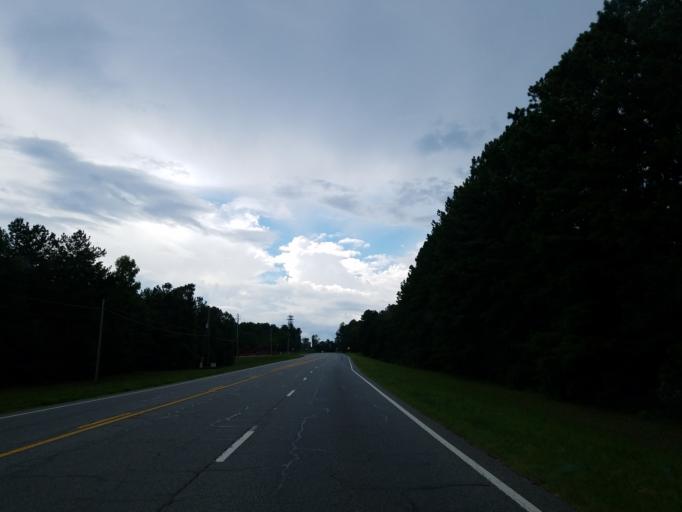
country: US
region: Georgia
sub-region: Bartow County
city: Adairsville
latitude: 34.3132
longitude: -84.8925
